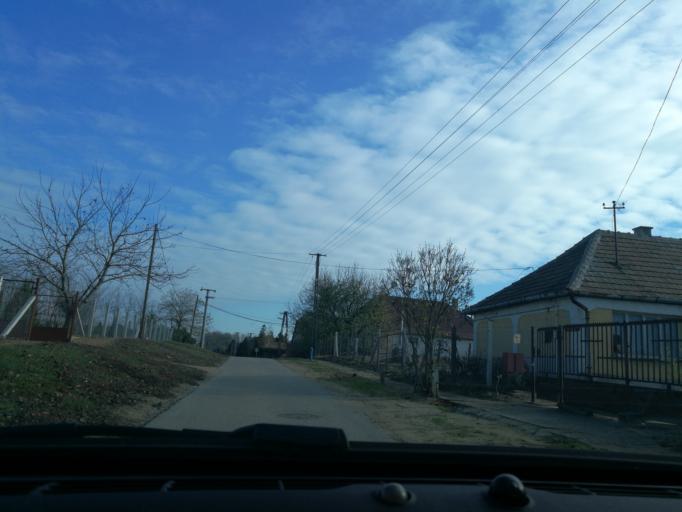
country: HU
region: Szabolcs-Szatmar-Bereg
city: Nyirpazony
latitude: 47.9603
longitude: 21.7846
